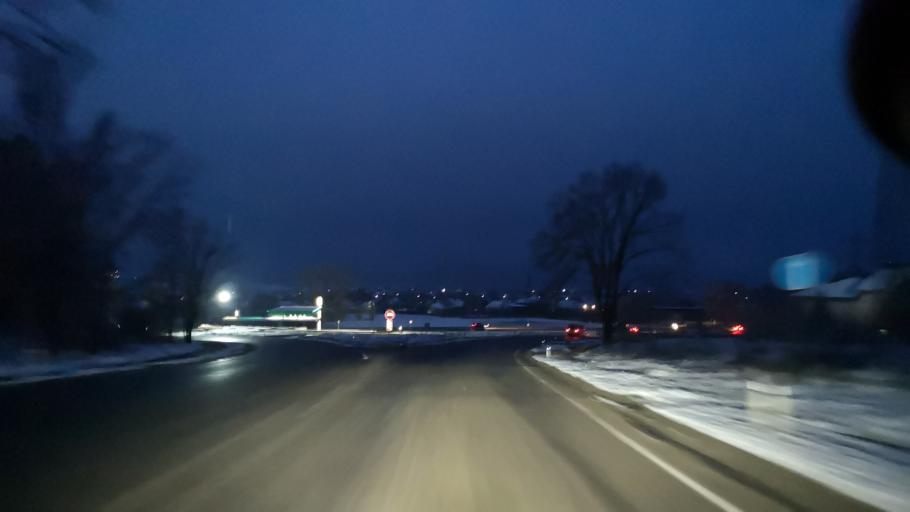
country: MD
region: Orhei
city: Orhei
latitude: 47.3940
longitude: 28.7977
